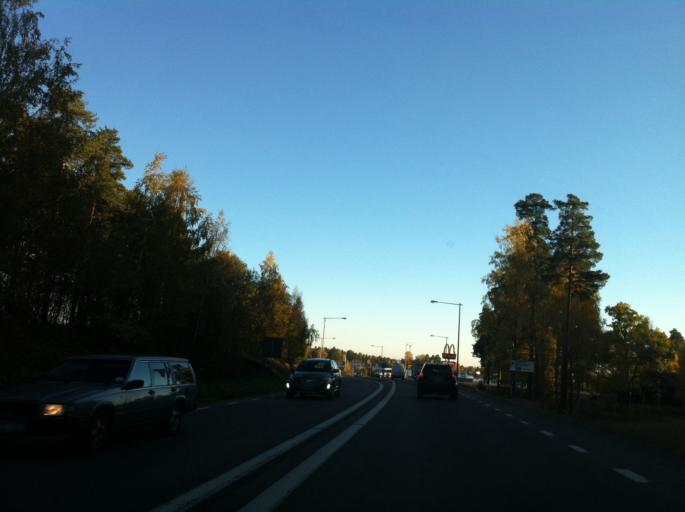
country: SE
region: Dalarna
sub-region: Faluns Kommun
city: Falun
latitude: 60.6111
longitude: 15.6533
